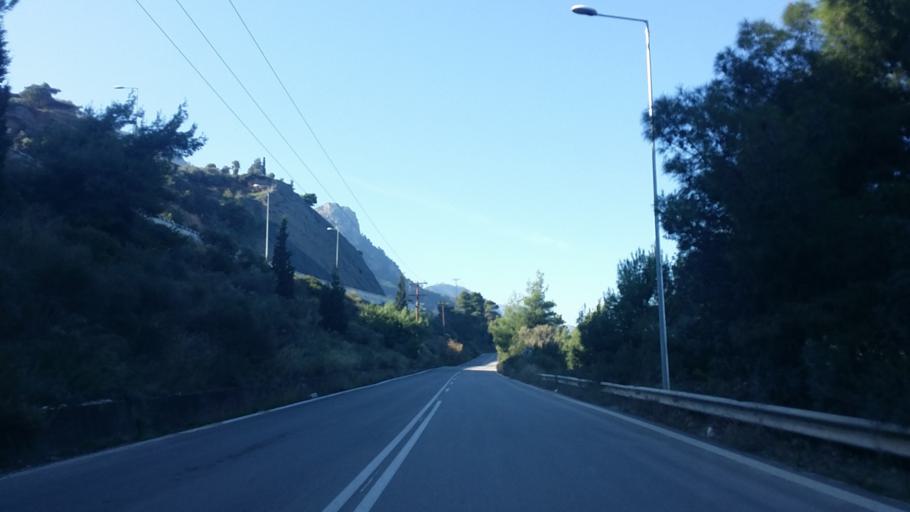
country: GR
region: West Greece
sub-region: Nomos Achaias
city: Akrata
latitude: 38.1774
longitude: 22.2337
